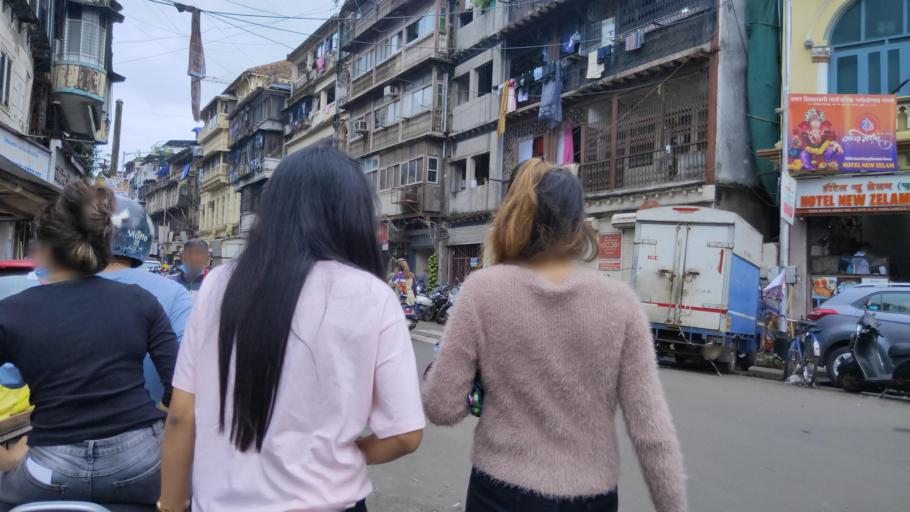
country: IN
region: Maharashtra
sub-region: Mumbai Suburban
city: Mumbai
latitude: 18.9548
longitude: 72.8258
